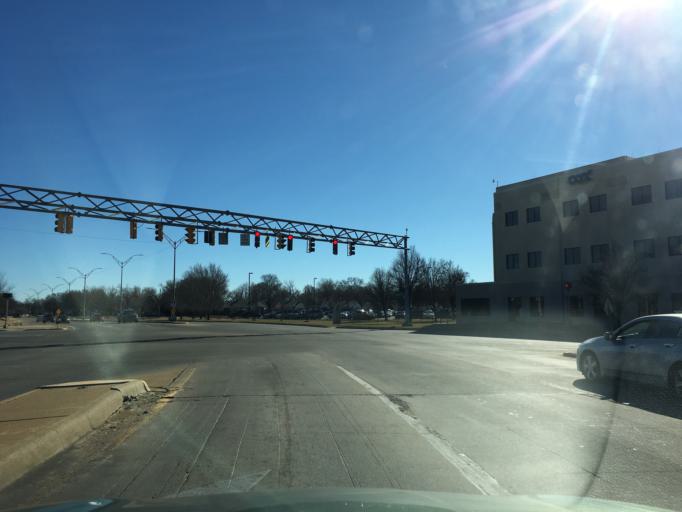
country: US
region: Kansas
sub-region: Sedgwick County
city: Wichita
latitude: 37.6722
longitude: -97.3082
